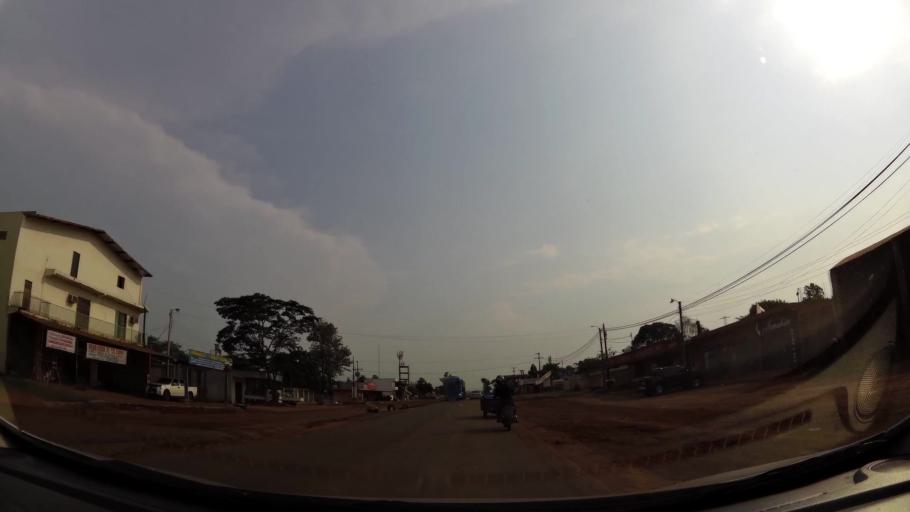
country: PY
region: Alto Parana
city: Ciudad del Este
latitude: -25.4834
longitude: -54.6595
